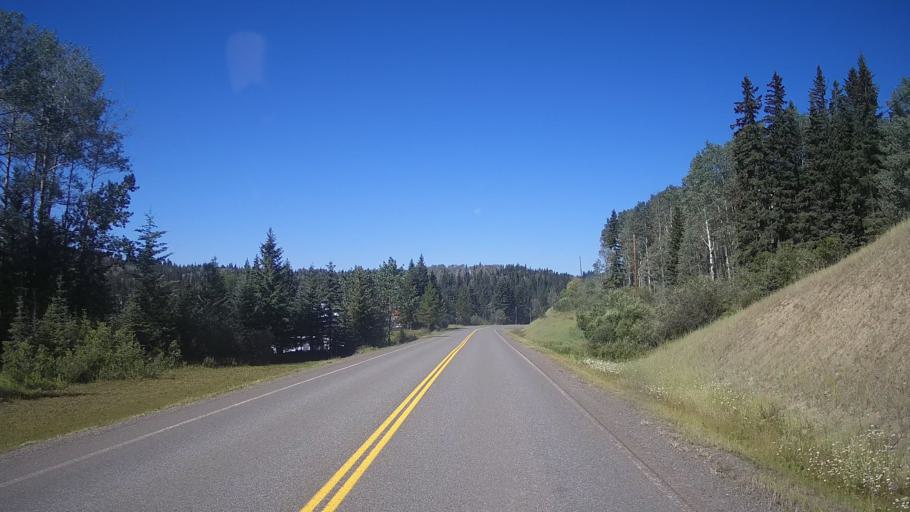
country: CA
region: British Columbia
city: Kamloops
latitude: 51.5030
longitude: -120.6230
